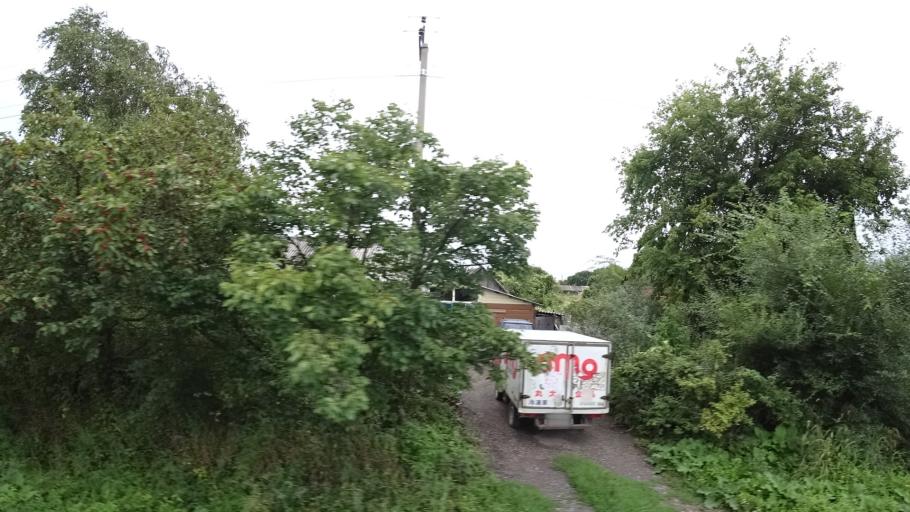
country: RU
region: Primorskiy
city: Chernigovka
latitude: 44.3371
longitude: 132.5933
